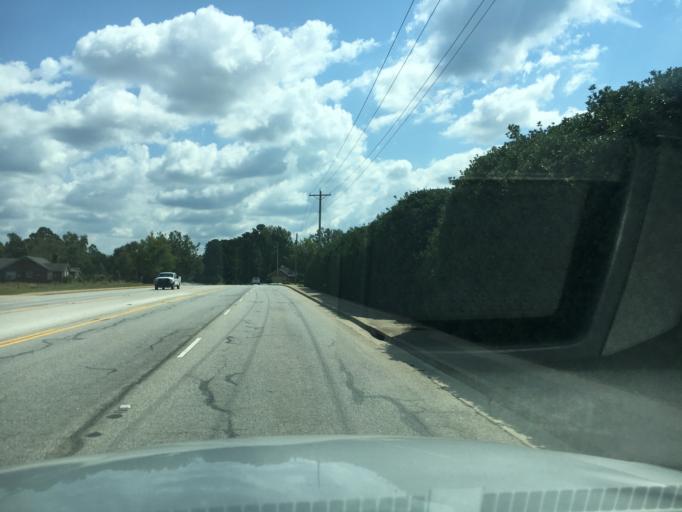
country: US
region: South Carolina
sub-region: Greenwood County
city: Greenwood
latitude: 34.1984
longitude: -82.1947
